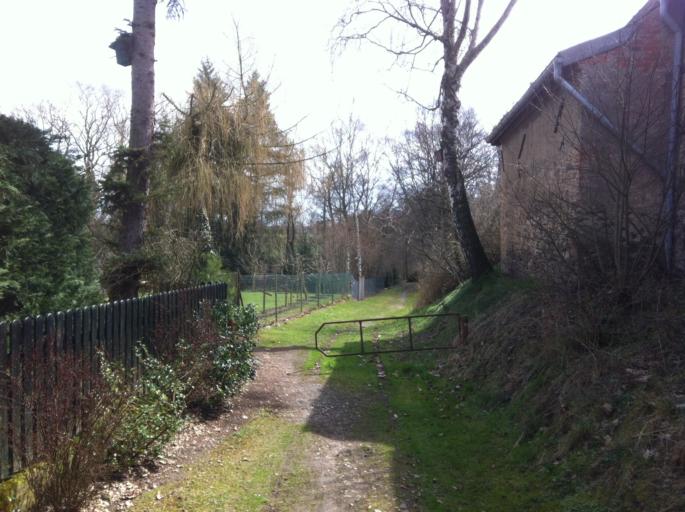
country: DE
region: Saxony
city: Trebsen
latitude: 51.3066
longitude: 12.7425
